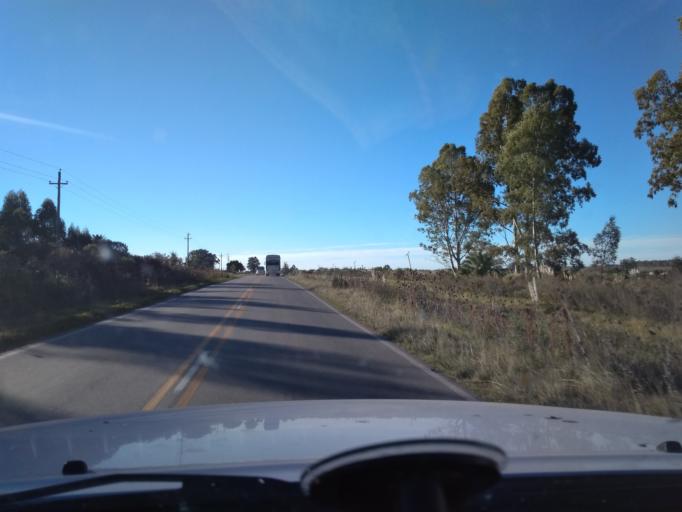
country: UY
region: Canelones
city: San Bautista
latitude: -34.4303
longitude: -55.9599
